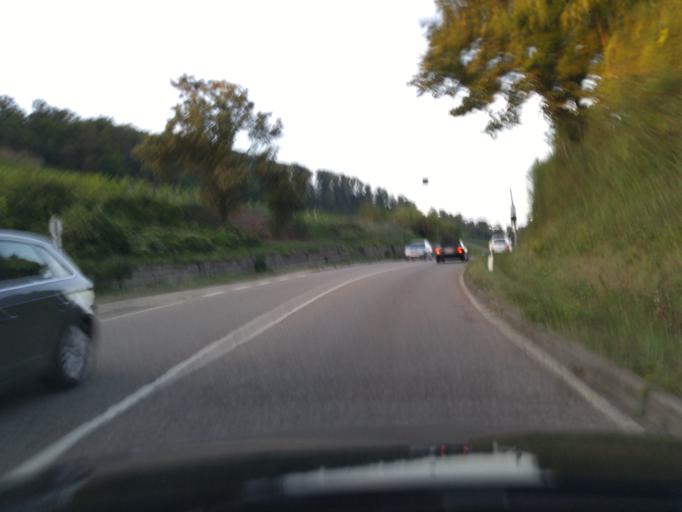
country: DE
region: Baden-Wuerttemberg
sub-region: Regierungsbezirk Stuttgart
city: Erlenbach
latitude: 49.1517
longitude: 9.2502
